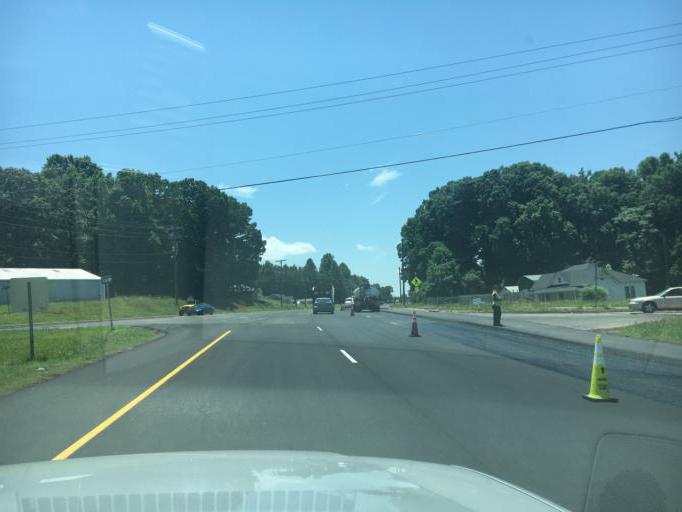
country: US
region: South Carolina
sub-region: Greenville County
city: Travelers Rest
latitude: 34.9461
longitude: -82.4394
